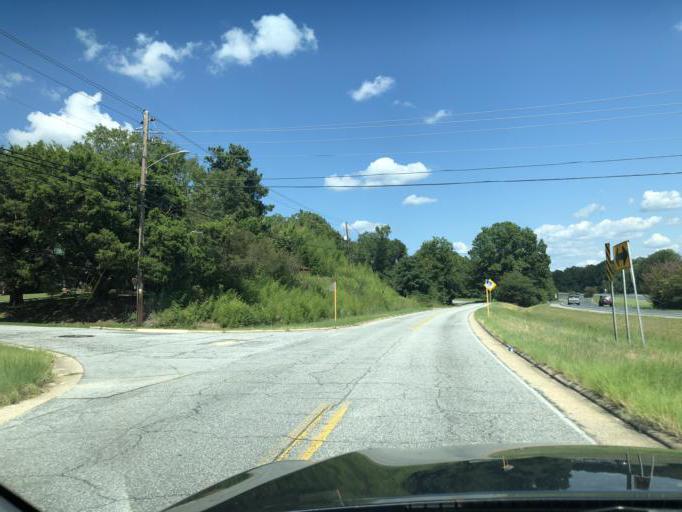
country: US
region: Georgia
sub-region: Muscogee County
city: Columbus
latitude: 32.5144
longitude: -84.9249
